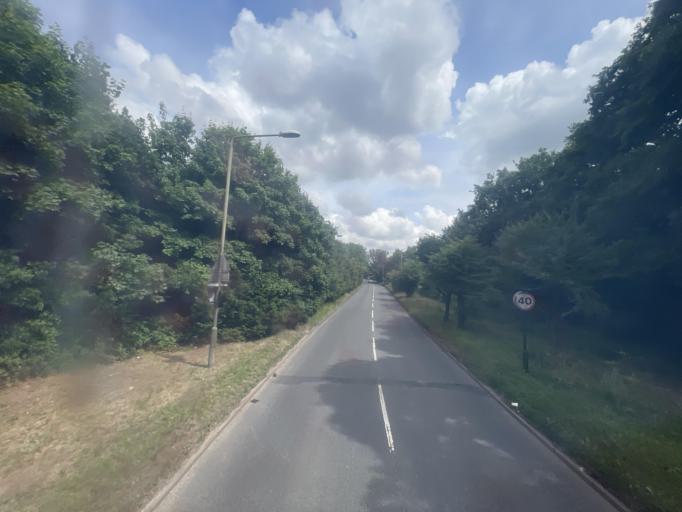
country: GB
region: England
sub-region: Greater London
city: West Wickham
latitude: 51.3695
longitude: 0.0102
